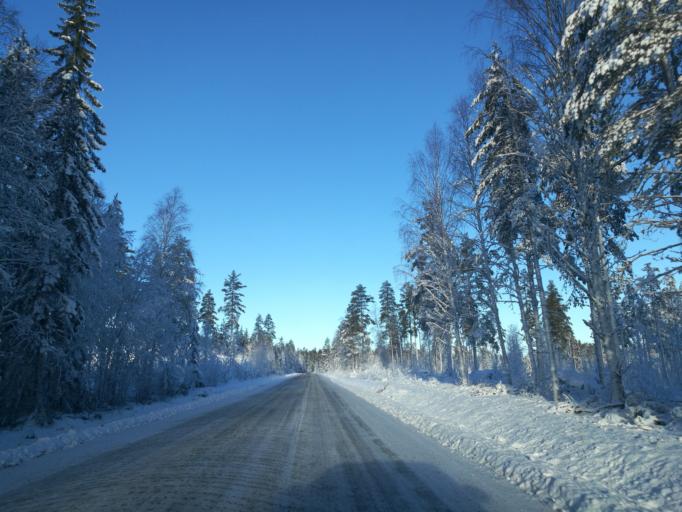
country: NO
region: Hedmark
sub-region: Grue
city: Kirkenaer
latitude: 60.5145
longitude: 12.5538
